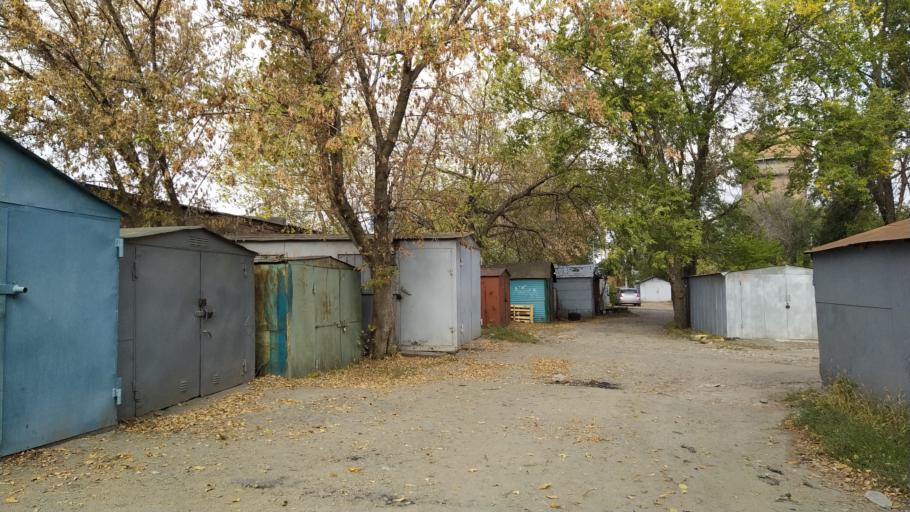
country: RU
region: Rostov
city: Bataysk
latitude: 47.1335
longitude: 39.7357
